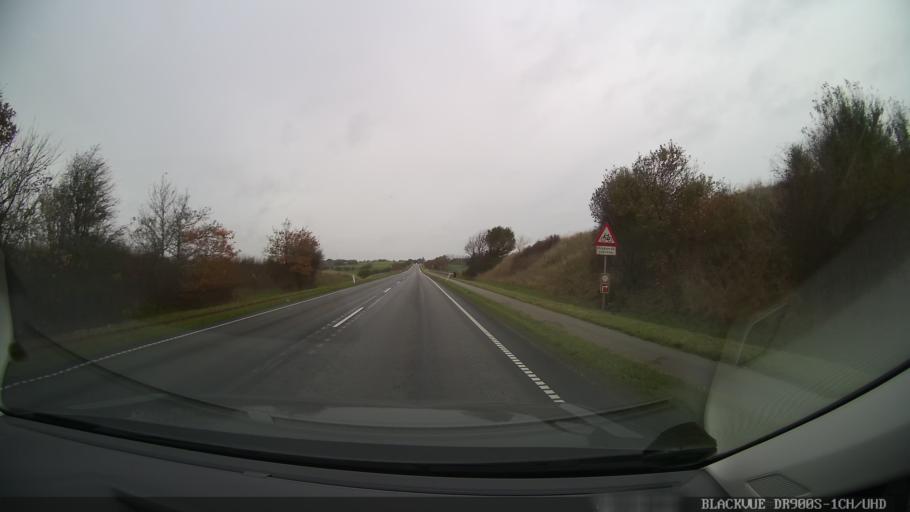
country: DK
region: North Denmark
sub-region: Thisted Kommune
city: Thisted
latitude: 56.8680
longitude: 8.6791
